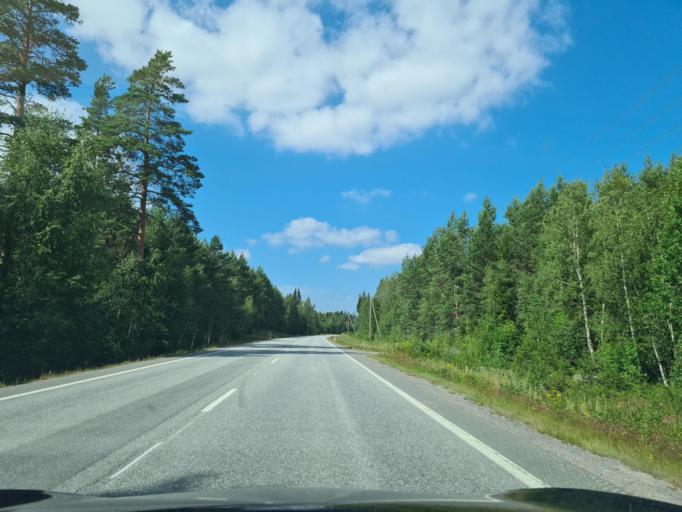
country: FI
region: Ostrobothnia
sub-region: Vaasa
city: Vaasa
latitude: 63.1708
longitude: 21.5833
